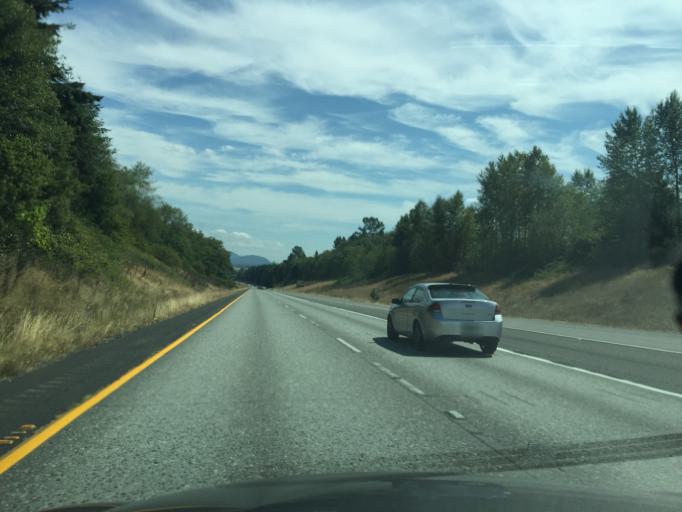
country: US
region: Washington
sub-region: Skagit County
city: Burlington
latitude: 48.5353
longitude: -122.3537
